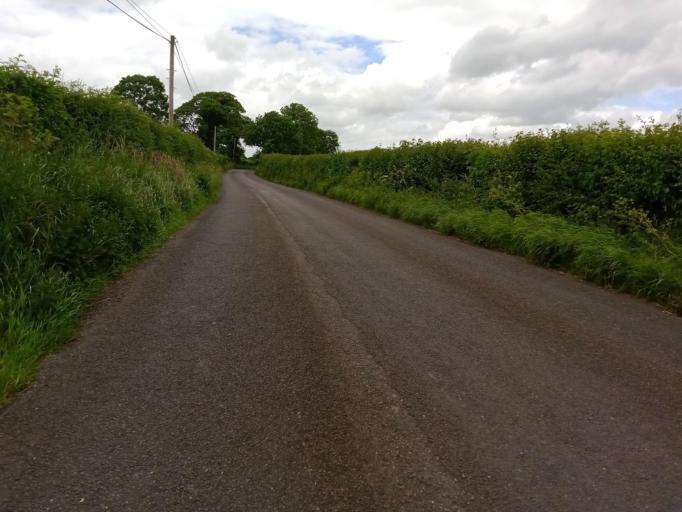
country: IE
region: Leinster
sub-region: Kilkenny
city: Kilkenny
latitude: 52.6890
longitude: -7.2494
